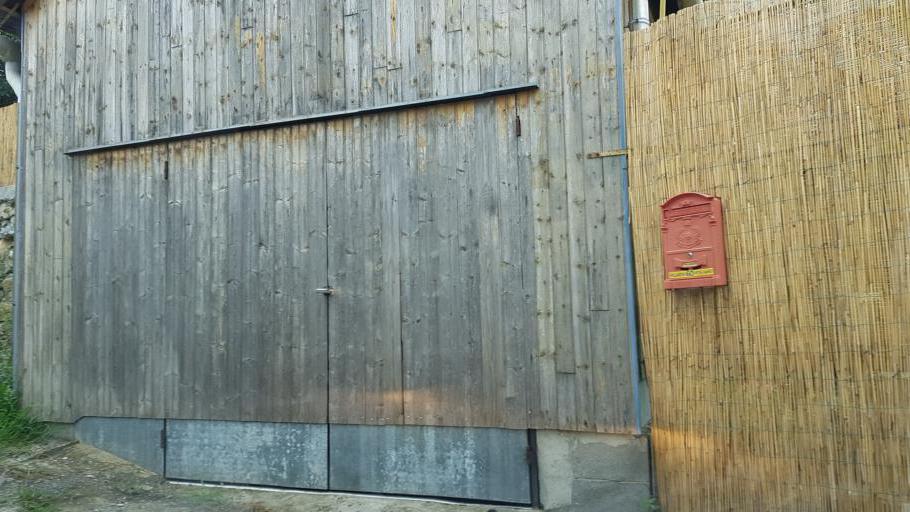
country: IT
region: Liguria
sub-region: Provincia di Genova
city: Piccarello
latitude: 44.4429
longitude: 9.0048
